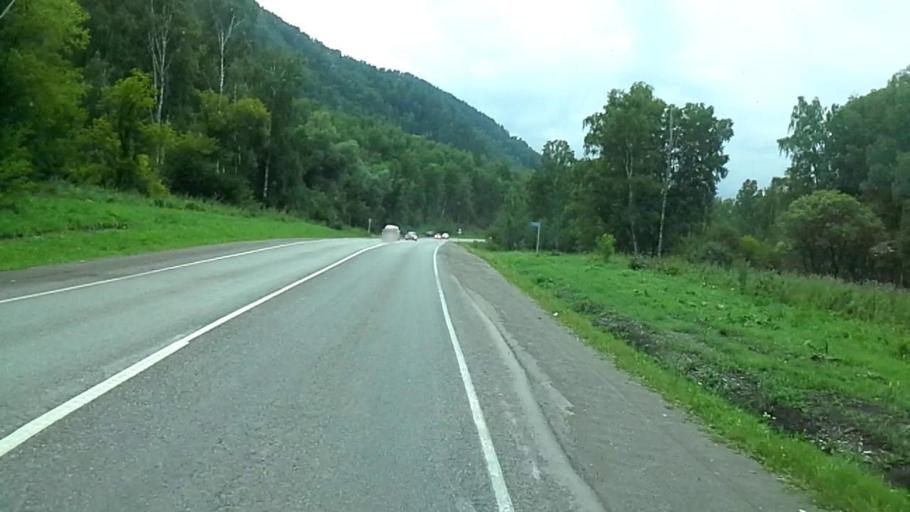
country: RU
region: Altay
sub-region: Mayminskiy Rayon
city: Manzherok
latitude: 51.8617
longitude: 85.7604
